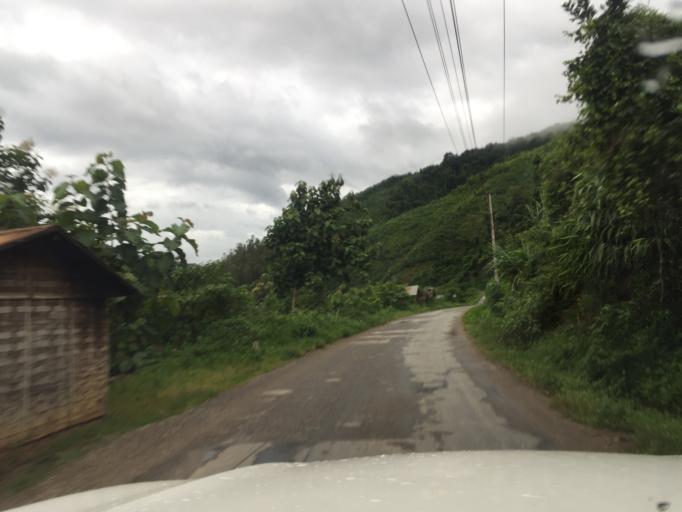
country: LA
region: Oudomxai
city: Muang La
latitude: 20.9801
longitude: 102.2249
